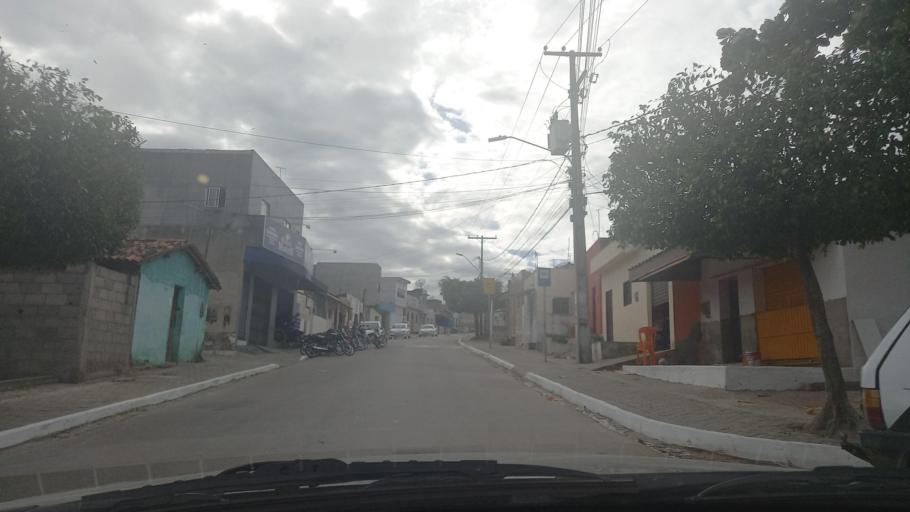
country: BR
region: Pernambuco
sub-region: Caruaru
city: Caruaru
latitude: -8.2963
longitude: -36.0294
